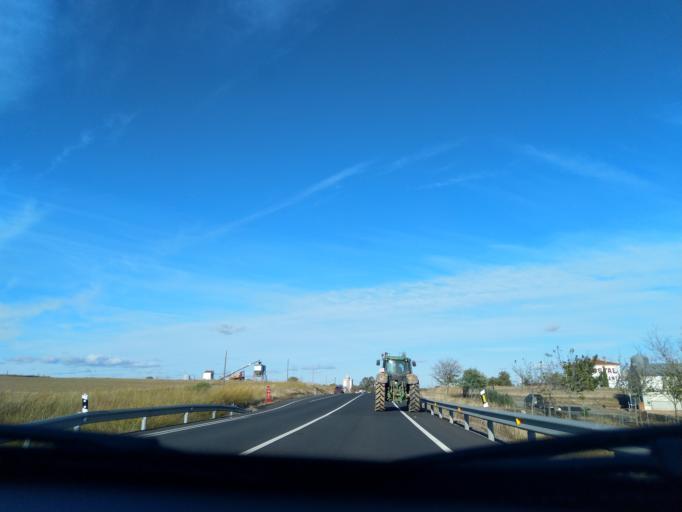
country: ES
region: Extremadura
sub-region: Provincia de Badajoz
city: Ahillones
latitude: 38.2713
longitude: -5.8346
